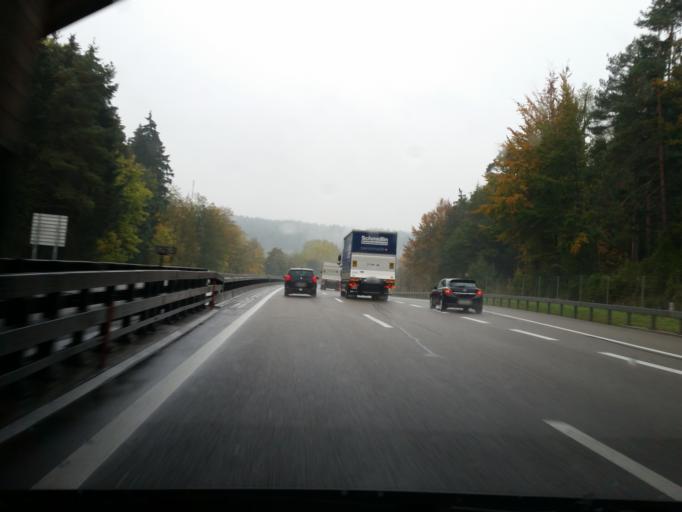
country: CH
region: Zurich
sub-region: Bezirk Winterthur
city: Veltheim
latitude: 47.5244
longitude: 8.7226
